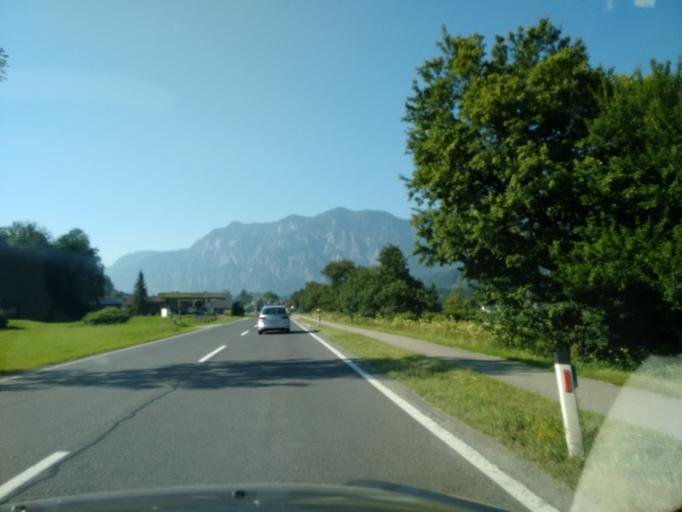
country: AT
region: Upper Austria
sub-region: Politischer Bezirk Gmunden
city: Bad Goisern
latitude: 47.6577
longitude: 13.6094
